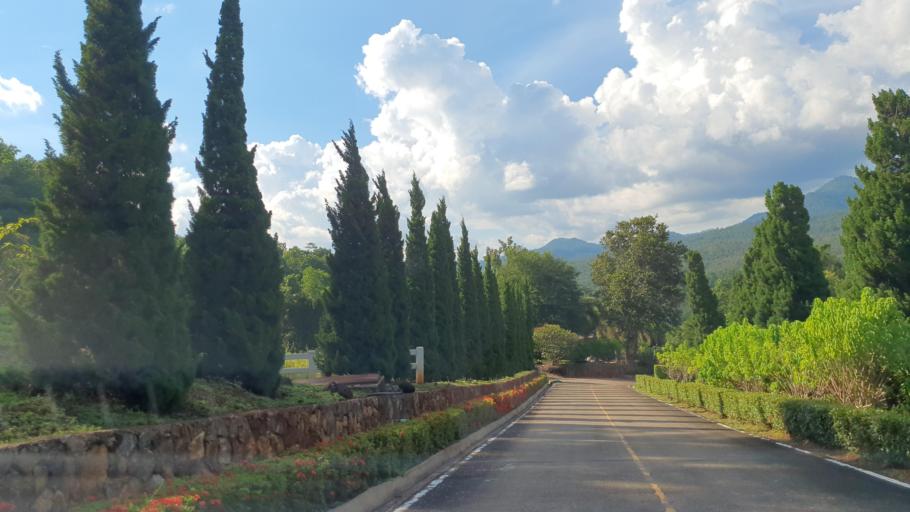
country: TH
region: Chiang Mai
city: Hang Dong
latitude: 18.7640
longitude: 98.8676
